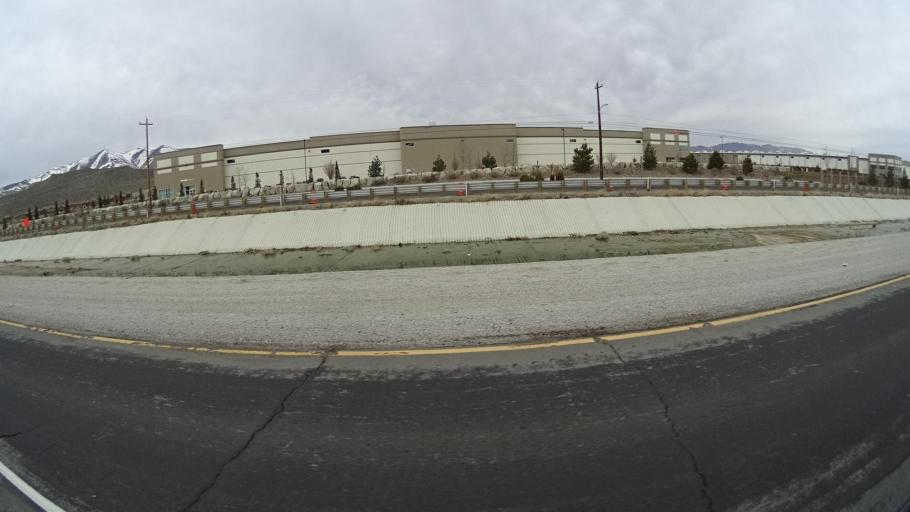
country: US
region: Nevada
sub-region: Washoe County
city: Lemmon Valley
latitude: 39.6300
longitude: -119.8457
